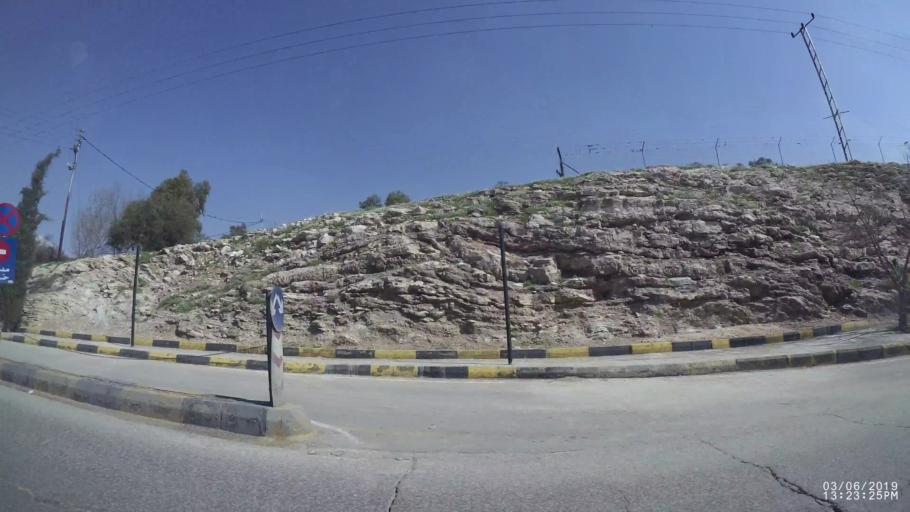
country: JO
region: Zarqa
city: Zarqa
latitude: 32.0548
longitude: 36.0947
